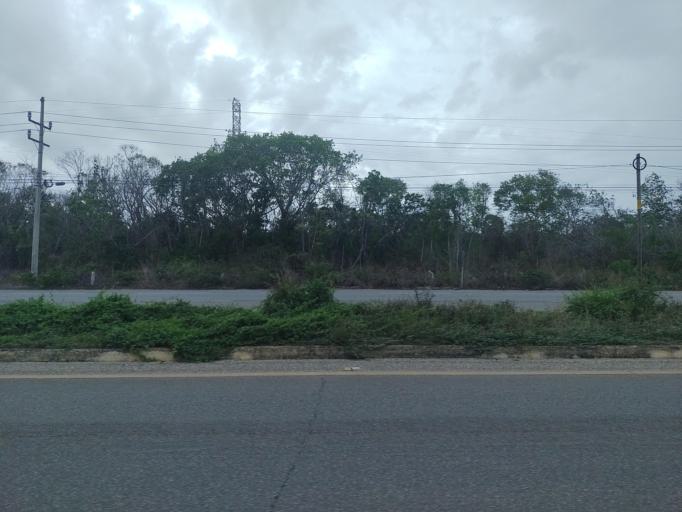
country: MX
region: Quintana Roo
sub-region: Tulum
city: Ciudad Chemuyil
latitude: 20.2768
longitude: -87.3940
